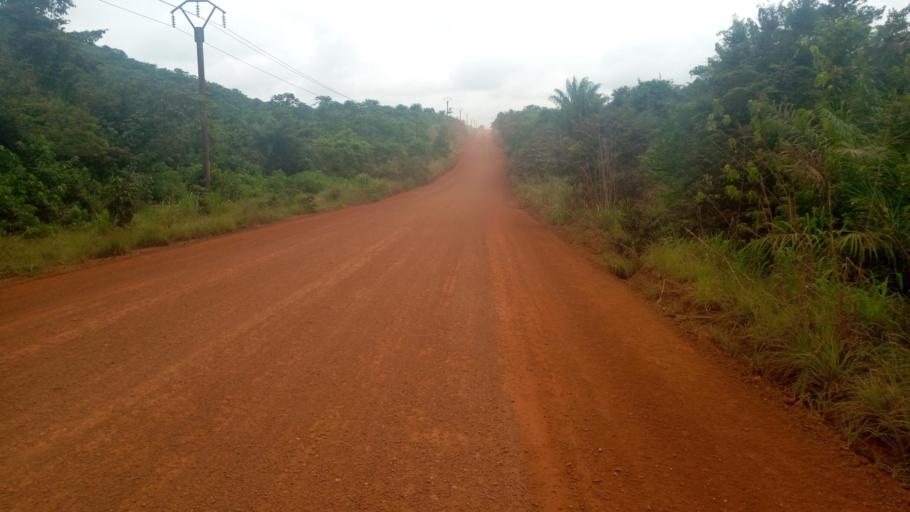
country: SL
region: Southern Province
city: Mogbwemo
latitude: 7.7104
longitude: -12.2849
